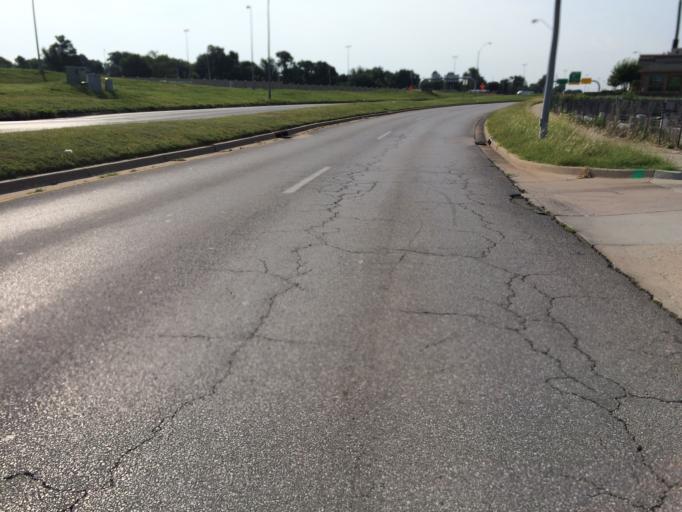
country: US
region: Oklahoma
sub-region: Cleveland County
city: Norman
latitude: 35.2165
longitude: -97.4869
